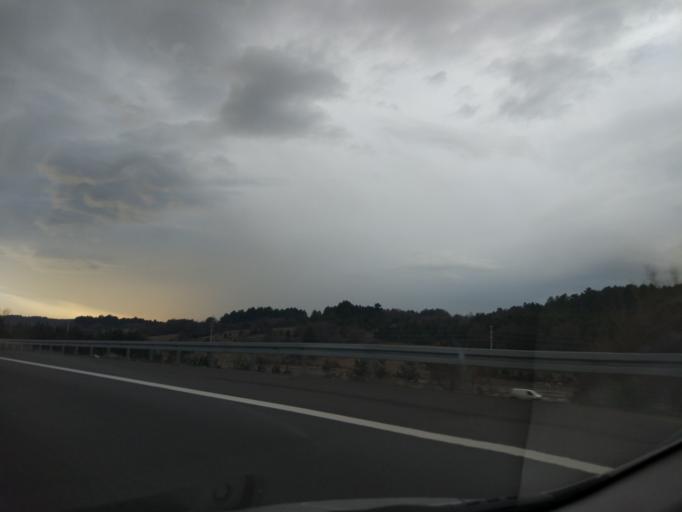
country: TR
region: Bolu
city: Yenicaga
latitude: 40.7544
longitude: 31.9133
